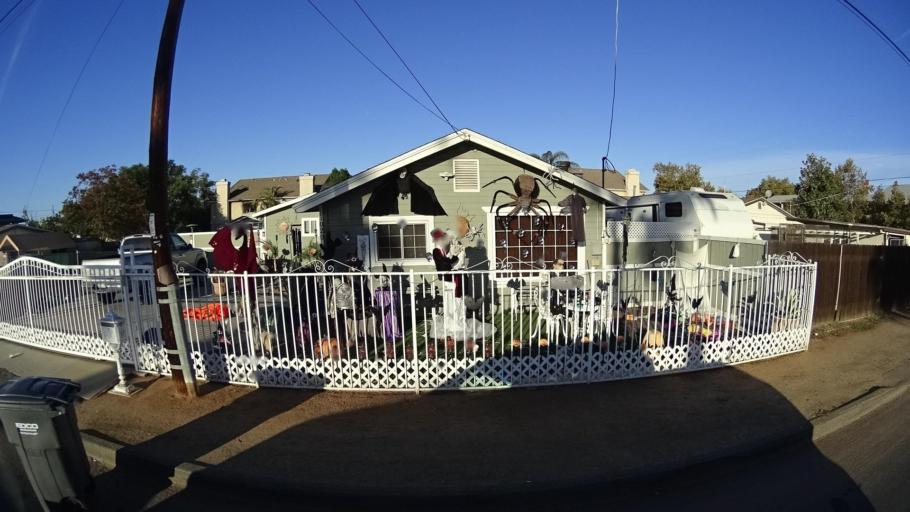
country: US
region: California
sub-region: San Diego County
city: Bostonia
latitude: 32.8095
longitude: -116.9379
